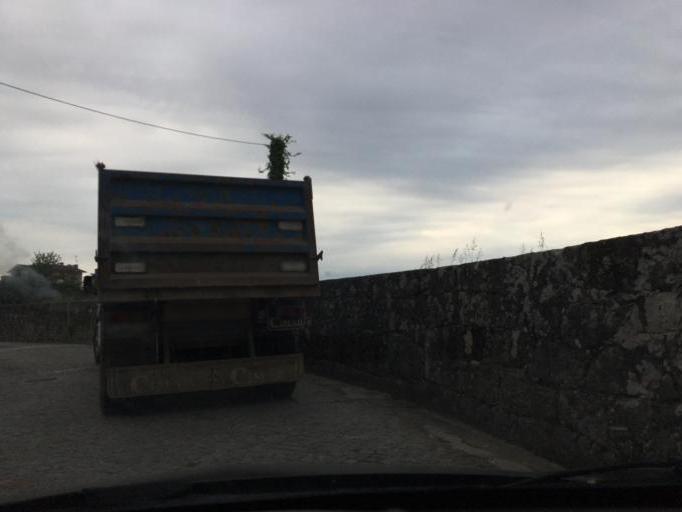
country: PT
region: Porto
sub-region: Maia
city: Anta
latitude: 41.2785
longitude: -8.6135
